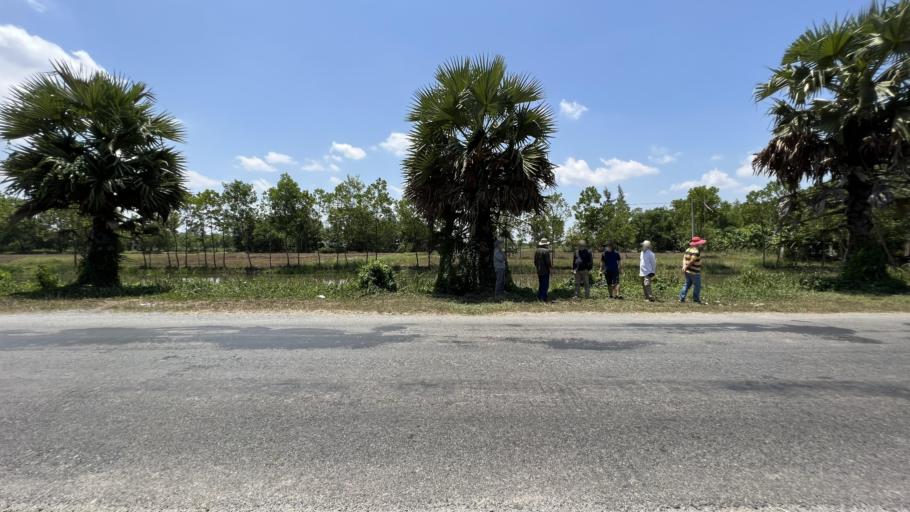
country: MM
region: Ayeyarwady
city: Kyaiklat
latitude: 16.3785
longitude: 95.8345
